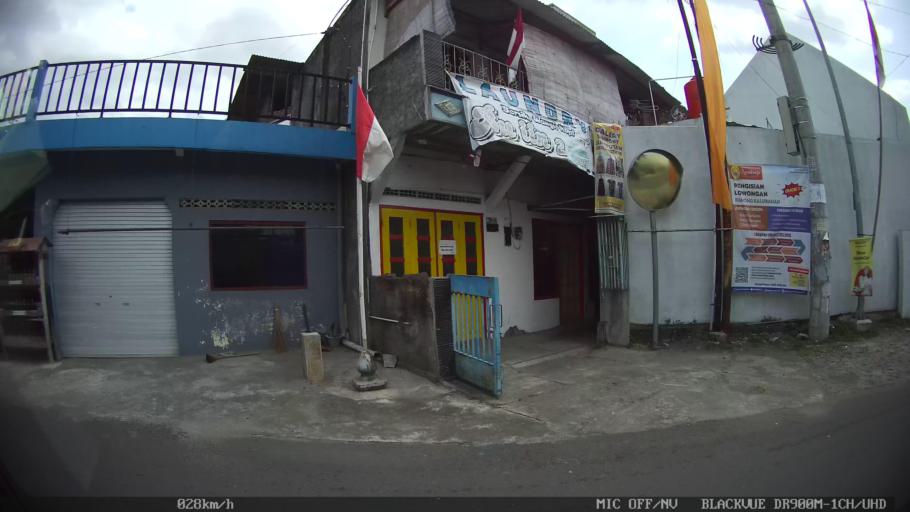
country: ID
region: Daerah Istimewa Yogyakarta
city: Gamping Lor
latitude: -7.8070
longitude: 110.3322
